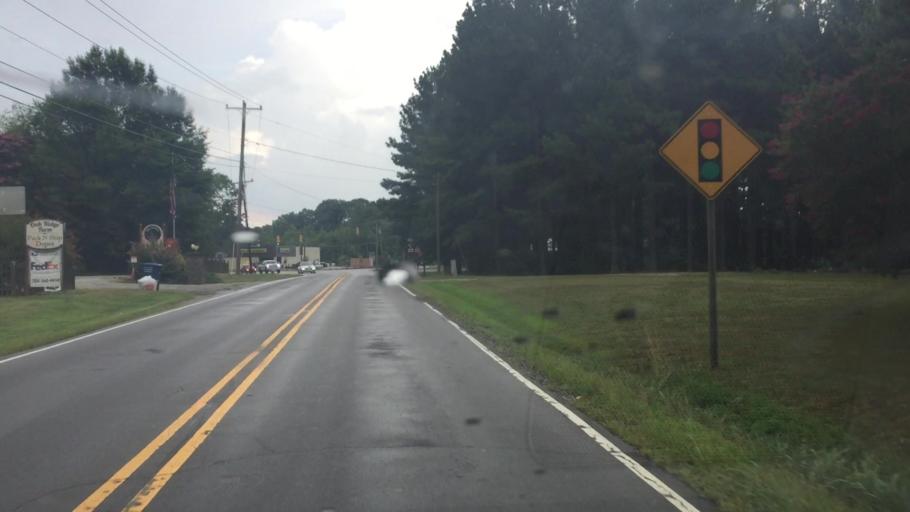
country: US
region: North Carolina
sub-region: Iredell County
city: Mooresville
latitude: 35.5986
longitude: -80.7661
